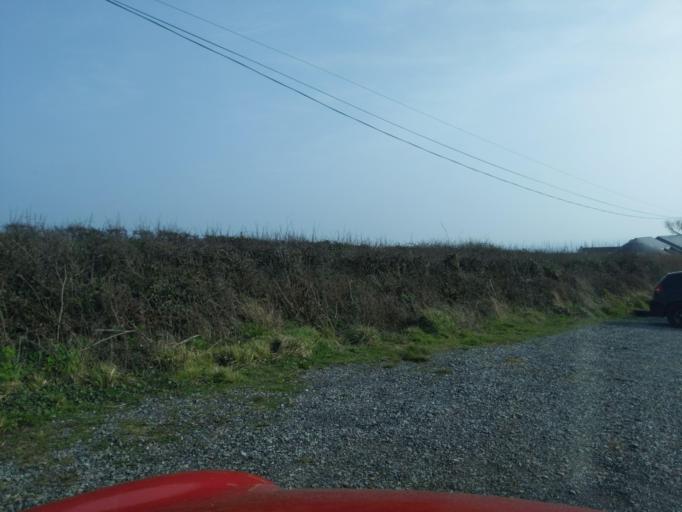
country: GB
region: England
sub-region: Devon
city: Salcombe
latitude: 50.2219
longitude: -3.7511
